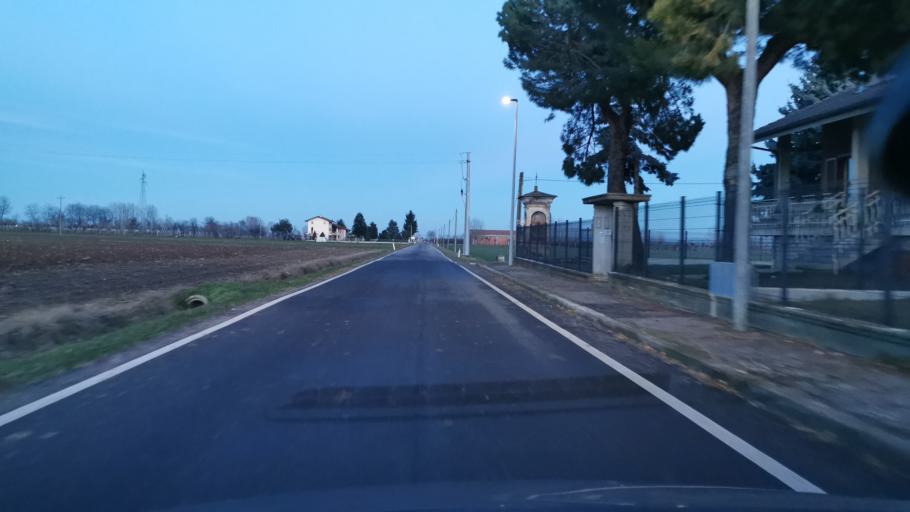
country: IT
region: Piedmont
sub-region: Provincia di Cuneo
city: Roata Rossi
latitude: 44.4548
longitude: 7.4934
